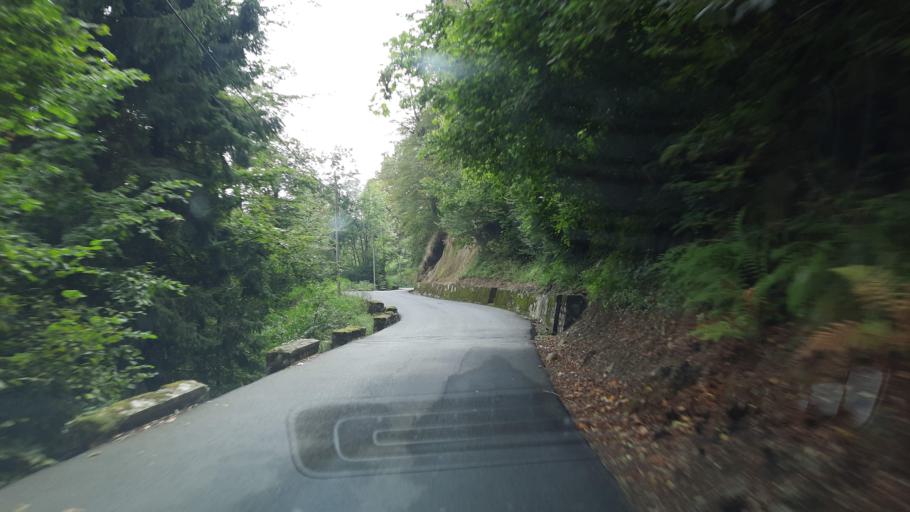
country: IT
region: Piedmont
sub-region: Provincia di Biella
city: Campiglia Cervo
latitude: 45.6609
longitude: 7.9985
